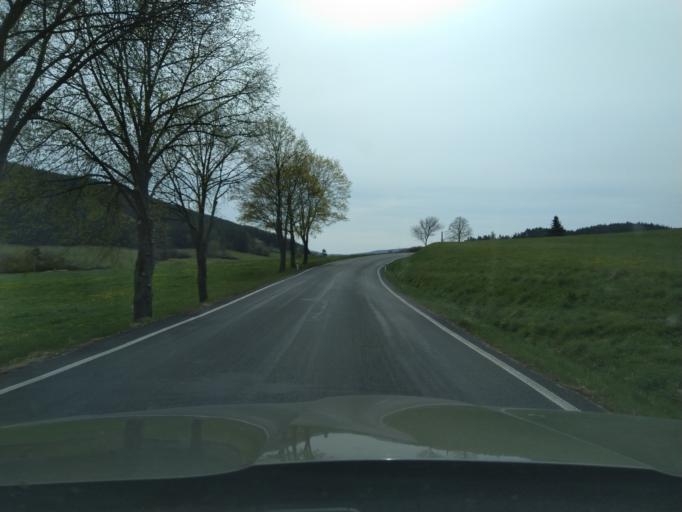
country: CZ
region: Plzensky
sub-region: Okres Klatovy
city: Susice
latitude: 49.2347
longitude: 13.5788
